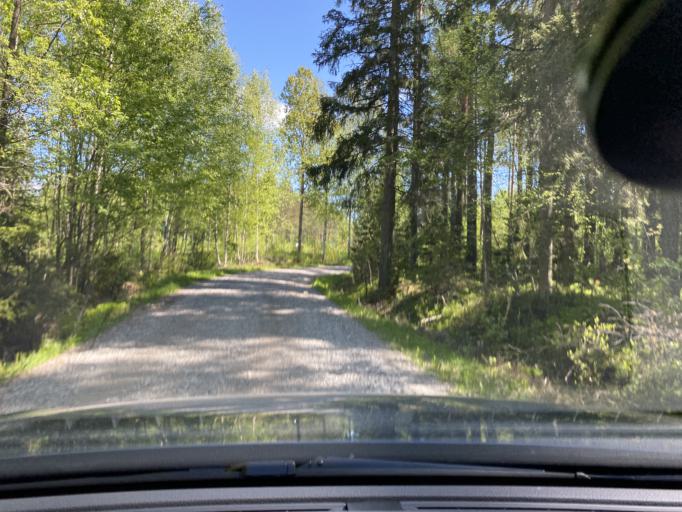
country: FI
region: Varsinais-Suomi
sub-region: Salo
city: Halikko
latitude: 60.3780
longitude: 22.9152
